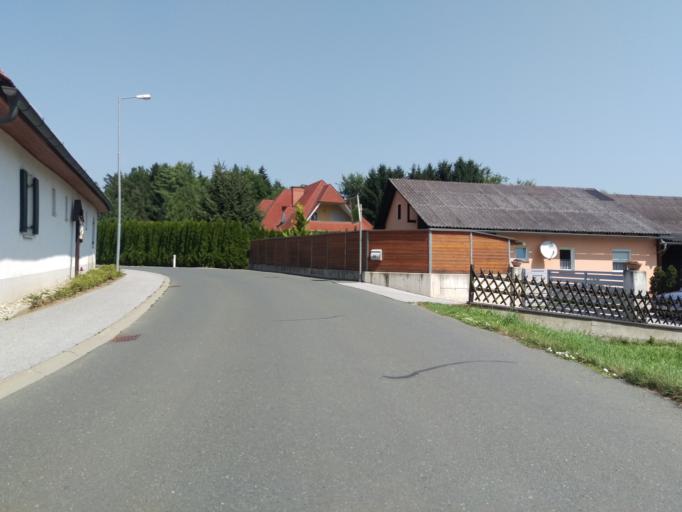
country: AT
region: Styria
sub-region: Politischer Bezirk Graz-Umgebung
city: Kalsdorf bei Graz
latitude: 46.9582
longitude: 15.4857
